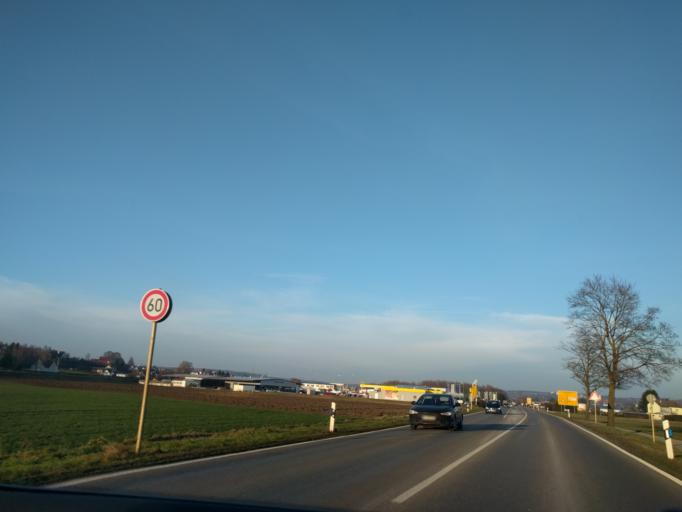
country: DE
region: Bavaria
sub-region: Swabia
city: Donauwoerth
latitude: 48.7032
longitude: 10.7490
